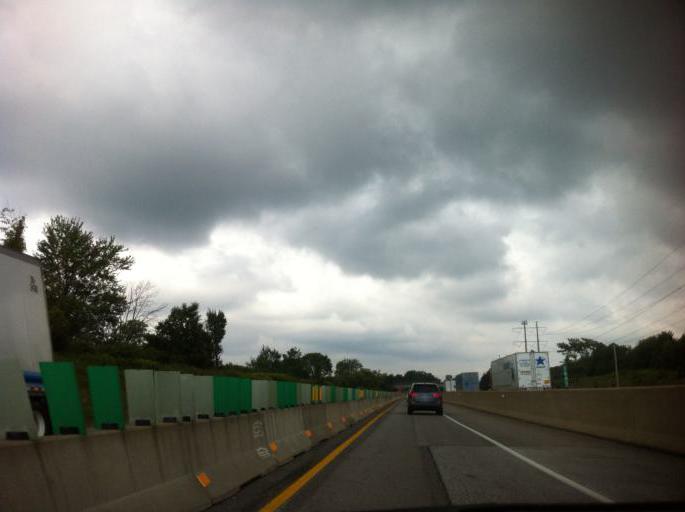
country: US
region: Ohio
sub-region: Cuyahoga County
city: North Royalton
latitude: 41.3170
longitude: -81.7696
